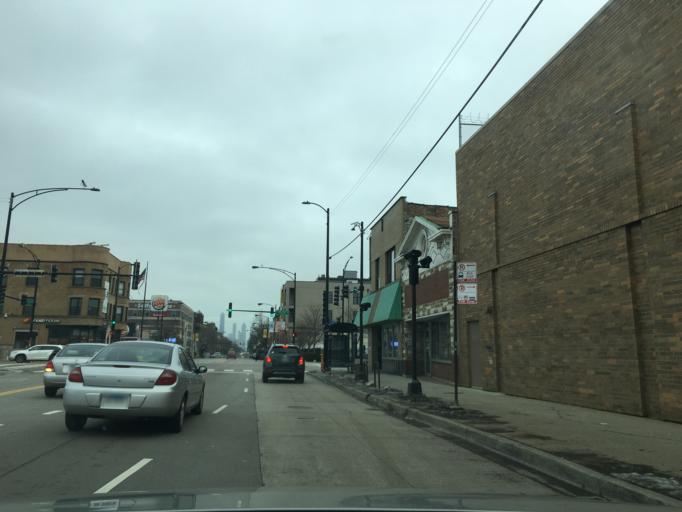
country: US
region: Illinois
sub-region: Cook County
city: Chicago
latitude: 41.8957
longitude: -87.6875
